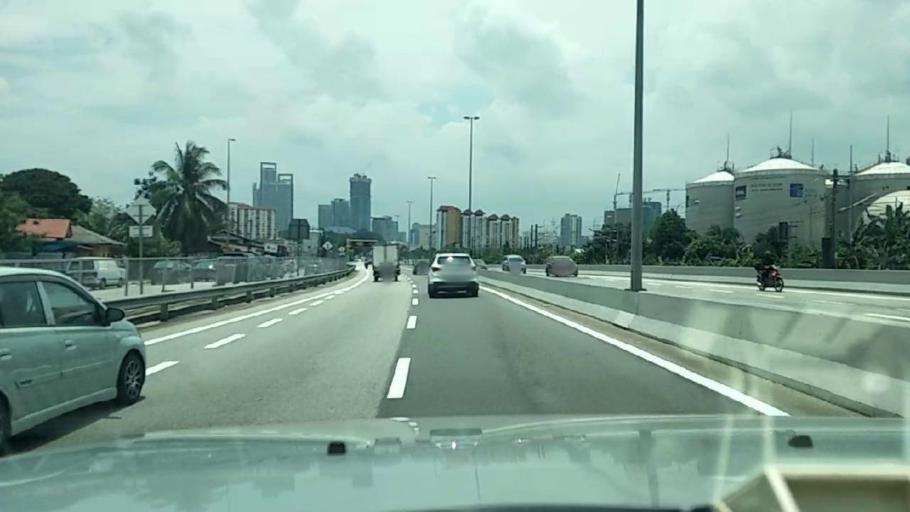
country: MY
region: Kuala Lumpur
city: Kuala Lumpur
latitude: 3.0982
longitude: 101.6704
